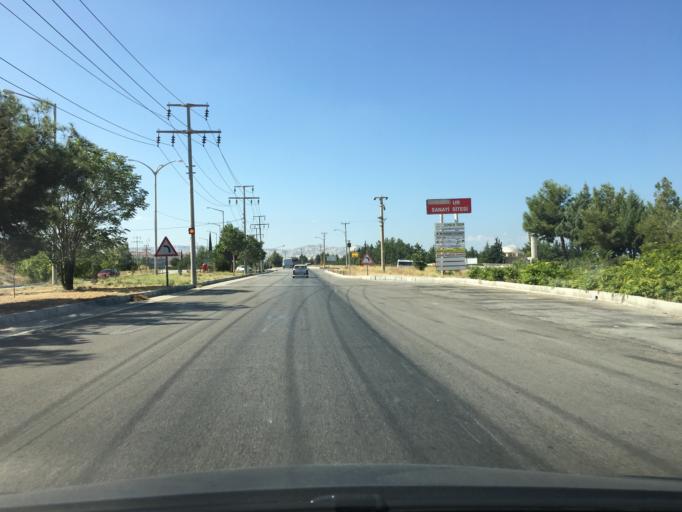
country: TR
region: Burdur
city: Burdur
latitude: 37.7437
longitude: 30.3156
